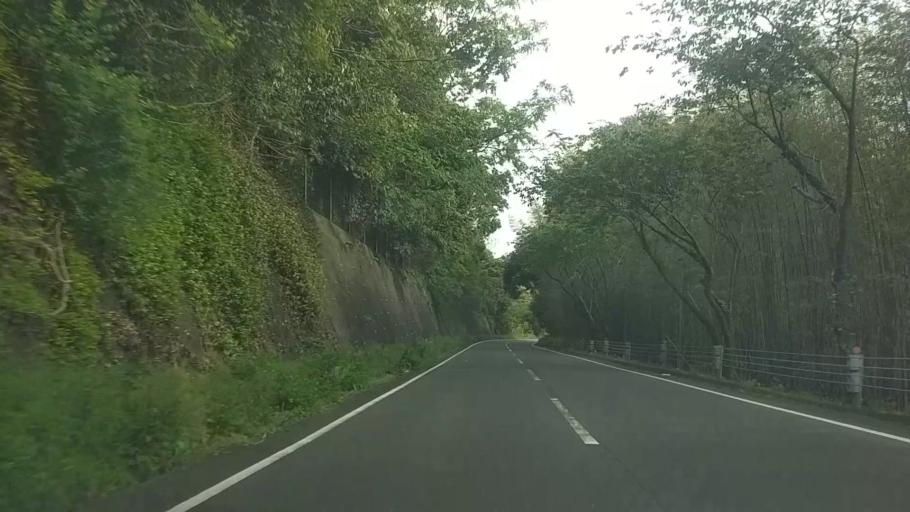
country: JP
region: Shizuoka
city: Kosai-shi
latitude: 34.7468
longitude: 137.5990
